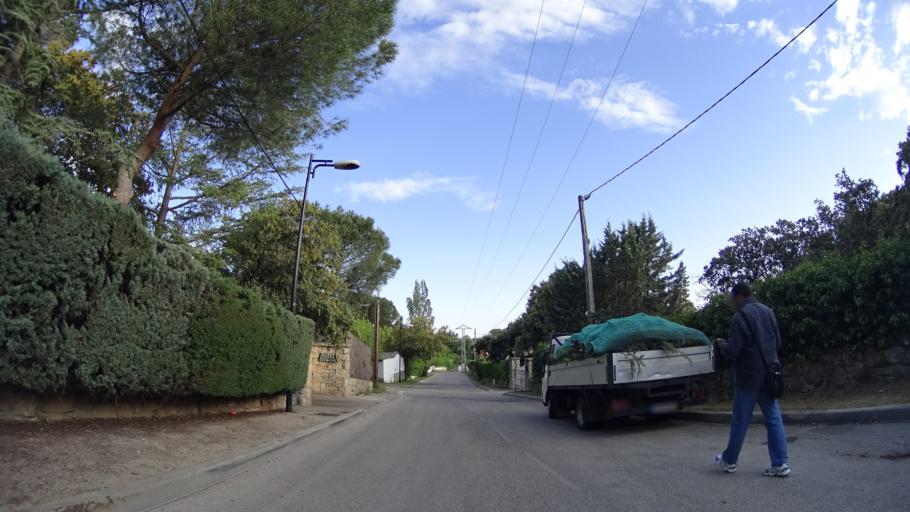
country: ES
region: Madrid
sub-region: Provincia de Madrid
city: Torrelodones
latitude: 40.5844
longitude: -3.9595
